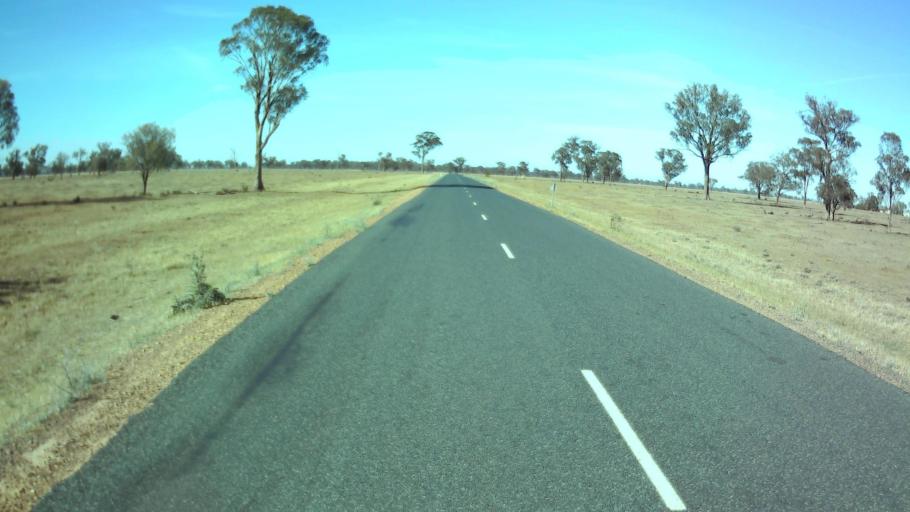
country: AU
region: New South Wales
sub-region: Weddin
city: Grenfell
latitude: -34.0464
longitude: 147.9239
